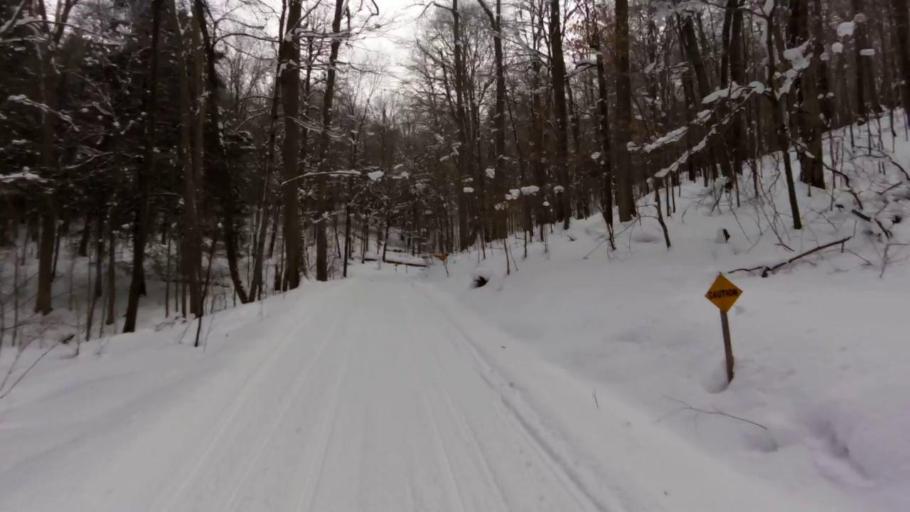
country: US
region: New York
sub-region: Cattaraugus County
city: Salamanca
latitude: 42.0596
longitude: -78.7785
